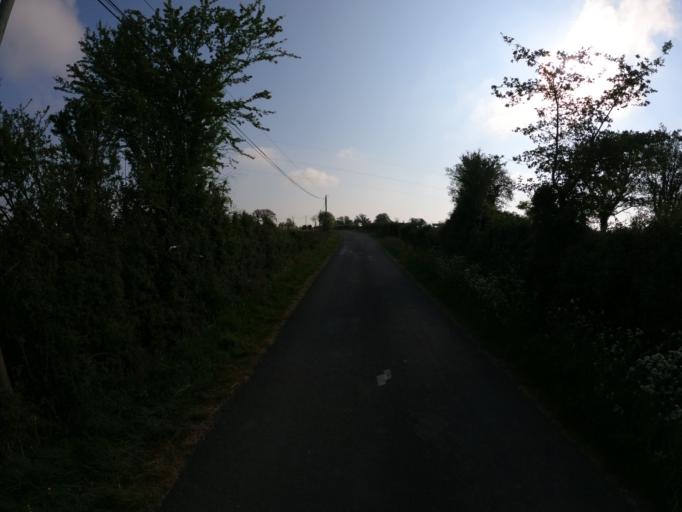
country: FR
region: Pays de la Loire
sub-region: Departement de Maine-et-Loire
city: La Romagne
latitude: 47.0732
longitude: -0.9969
